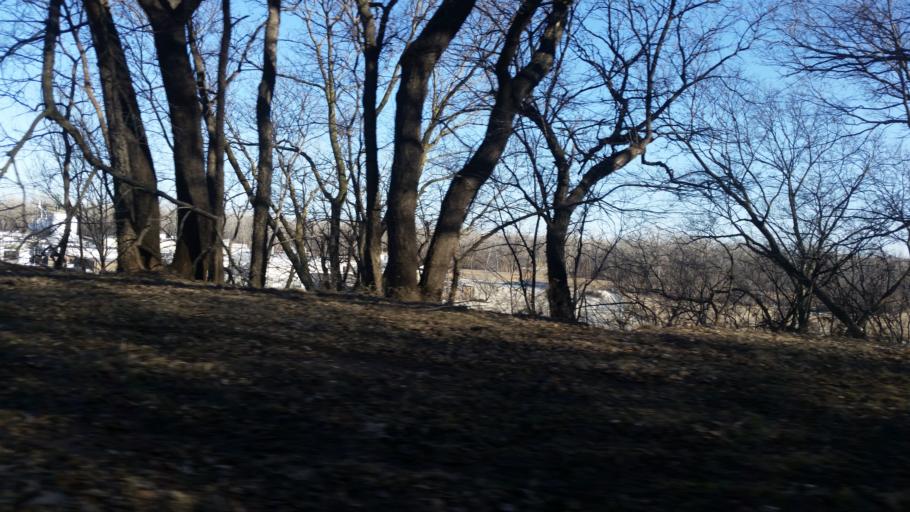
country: US
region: Nebraska
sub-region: Douglas County
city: Omaha
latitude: 41.2185
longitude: -95.9300
